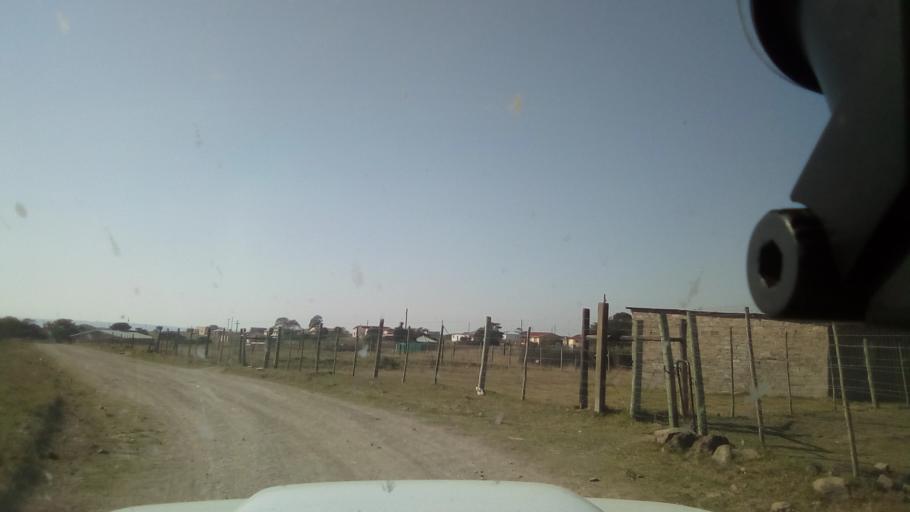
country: ZA
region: Eastern Cape
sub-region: Buffalo City Metropolitan Municipality
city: Bhisho
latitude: -32.9393
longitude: 27.3334
